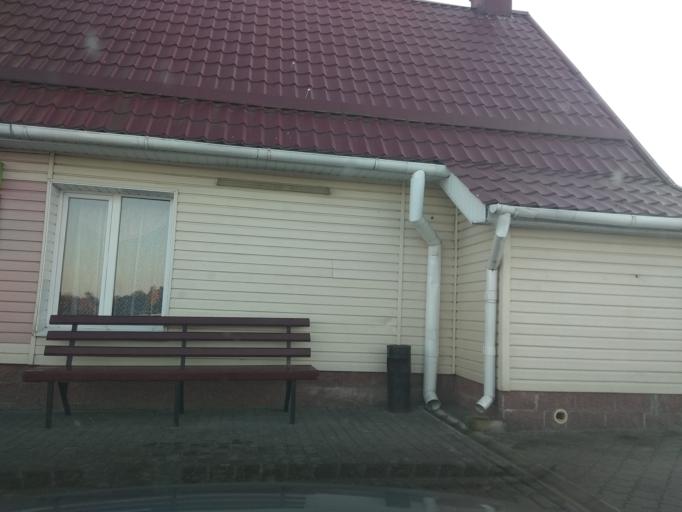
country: BY
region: Grodnenskaya
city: Zel'va
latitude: 53.1443
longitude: 24.8254
